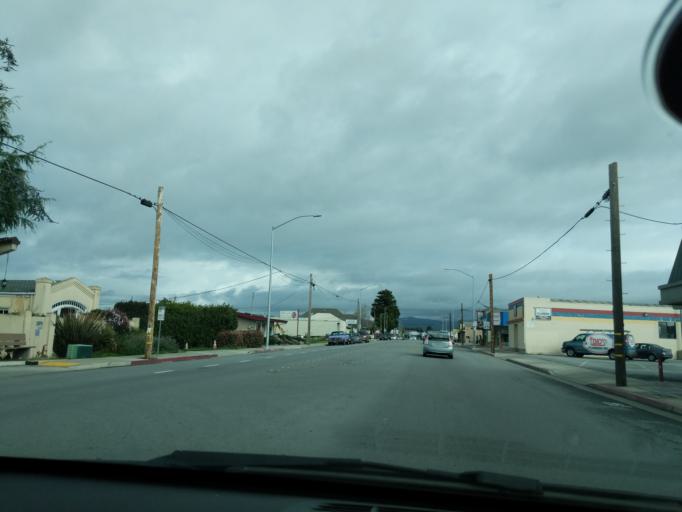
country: US
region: California
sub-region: Santa Cruz County
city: Watsonville
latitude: 36.9207
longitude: -121.7608
